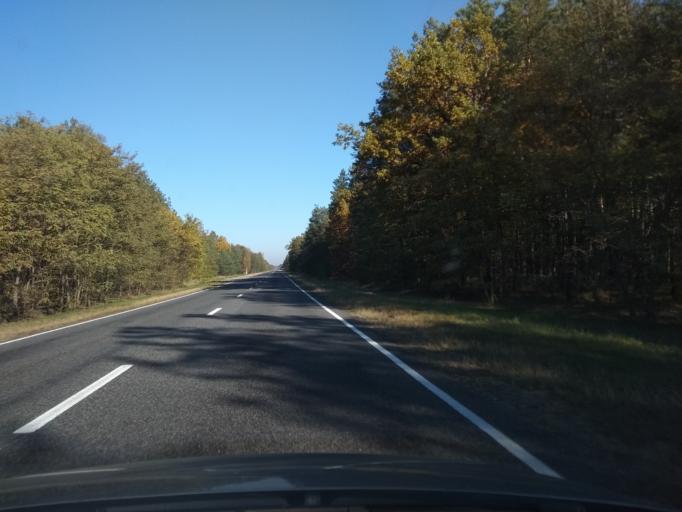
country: BY
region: Brest
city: Malaryta
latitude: 51.9699
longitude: 24.1970
